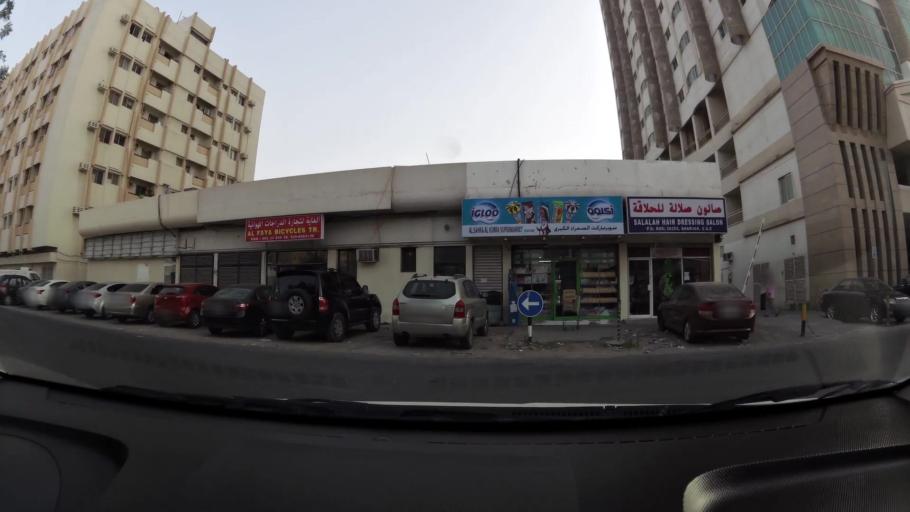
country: AE
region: Ash Shariqah
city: Sharjah
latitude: 25.3413
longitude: 55.4016
